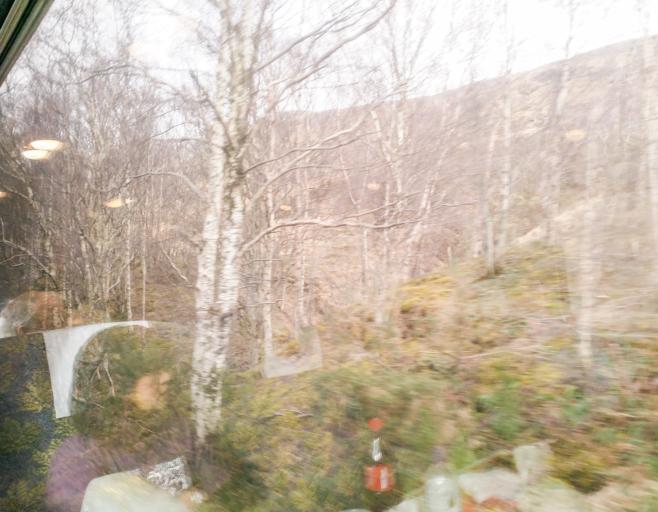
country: GB
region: Scotland
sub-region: Highland
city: Spean Bridge
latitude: 56.8176
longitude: -4.7141
